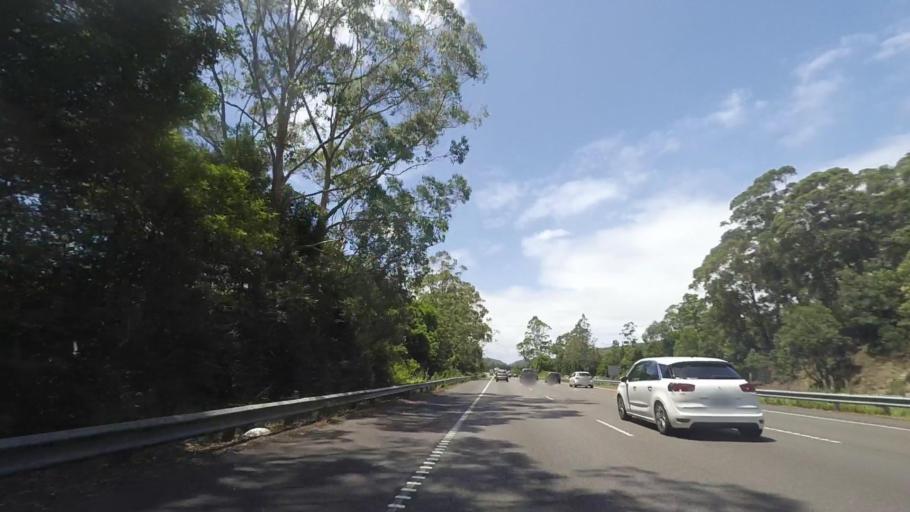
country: AU
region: New South Wales
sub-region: Gosford Shire
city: Lisarow
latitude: -33.3492
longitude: 151.3645
